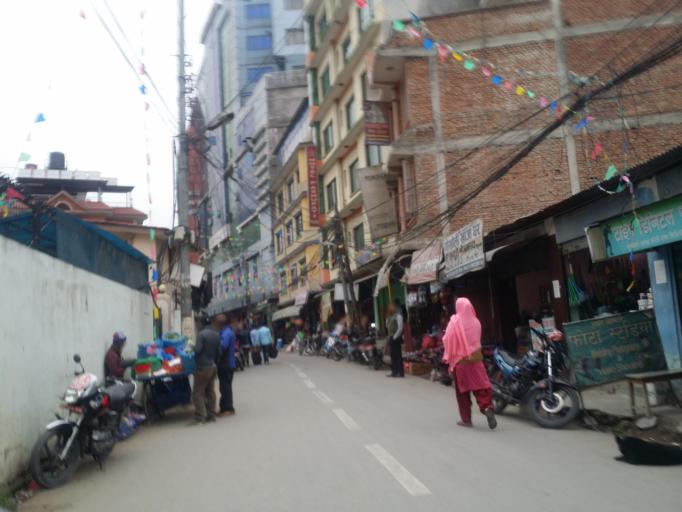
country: NP
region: Central Region
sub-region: Bagmati Zone
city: Kathmandu
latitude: 27.7048
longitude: 85.3479
